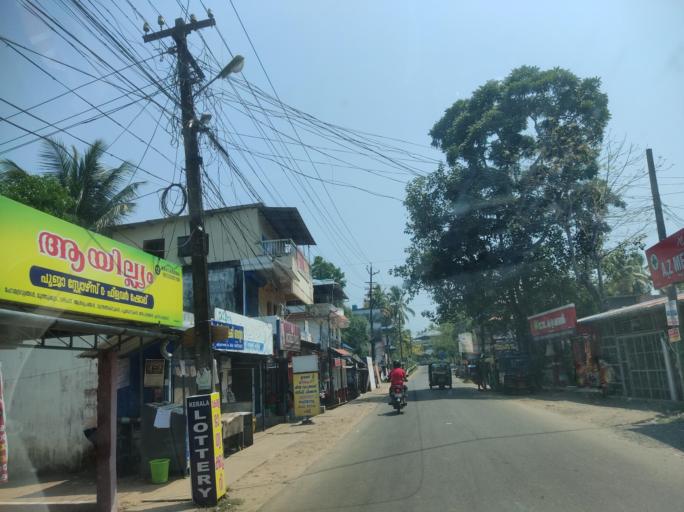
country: IN
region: Kerala
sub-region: Alappuzha
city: Kutiatodu
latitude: 9.7948
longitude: 76.3025
